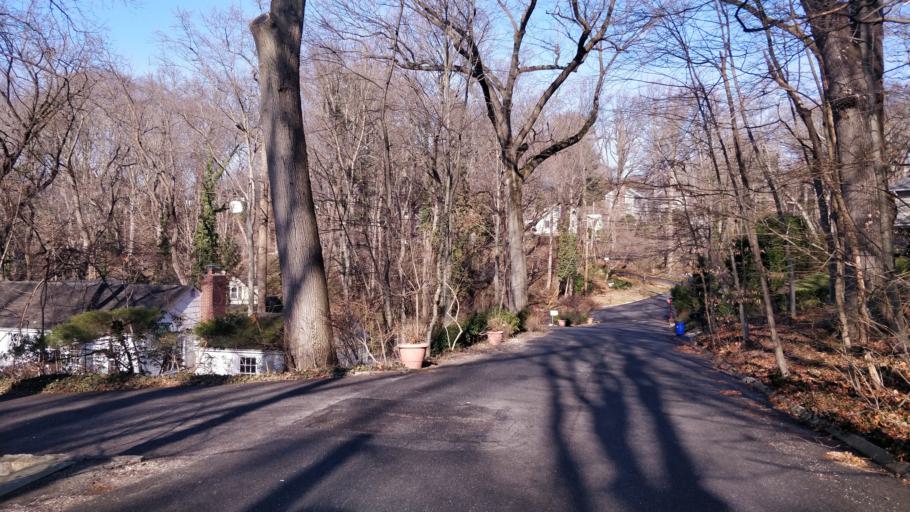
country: US
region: New York
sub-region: Nassau County
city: Sea Cliff
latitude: 40.8390
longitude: -73.6473
